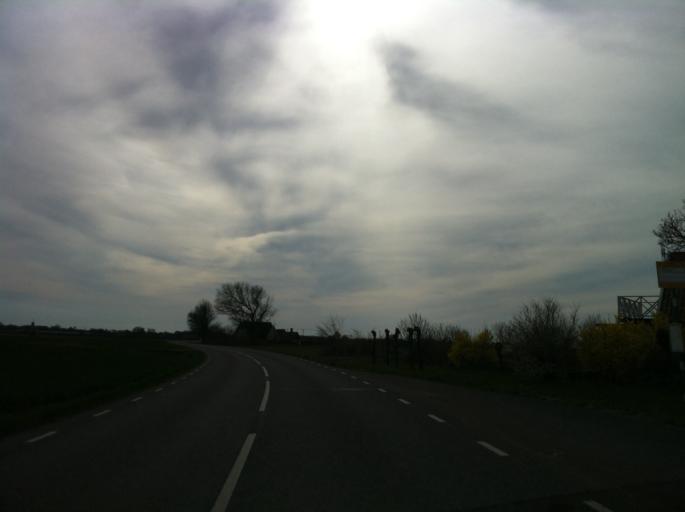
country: SE
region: Skane
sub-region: Hoganas Kommun
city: Hoganas
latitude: 56.2495
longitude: 12.5618
